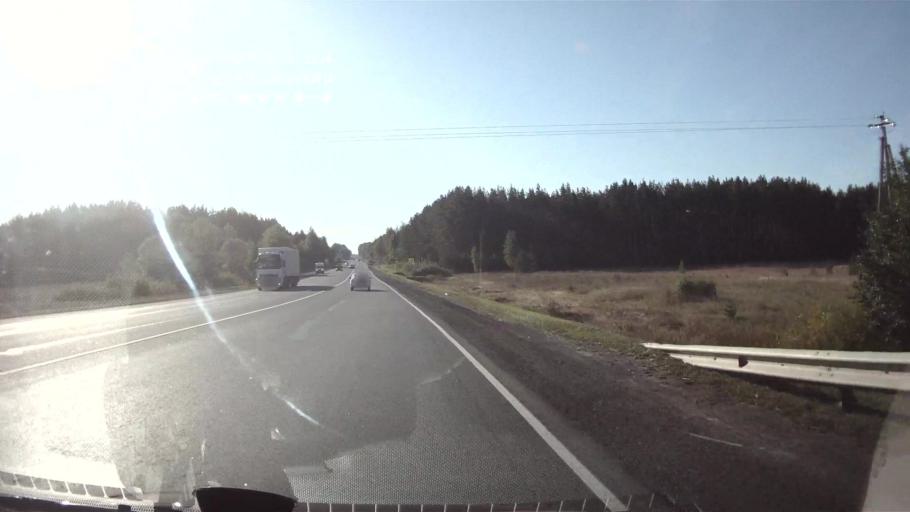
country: RU
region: Chuvashia
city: Shikhazany
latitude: 55.5558
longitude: 47.4093
